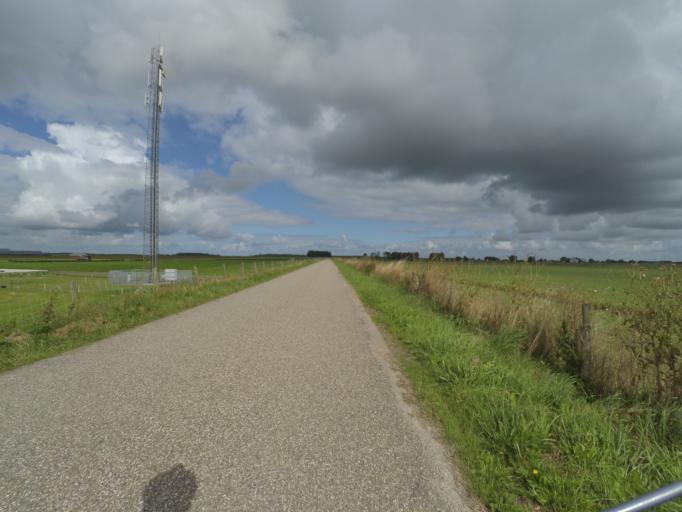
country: NL
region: Groningen
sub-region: Gemeente Zuidhorn
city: Grijpskerk
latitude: 53.3088
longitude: 6.2650
